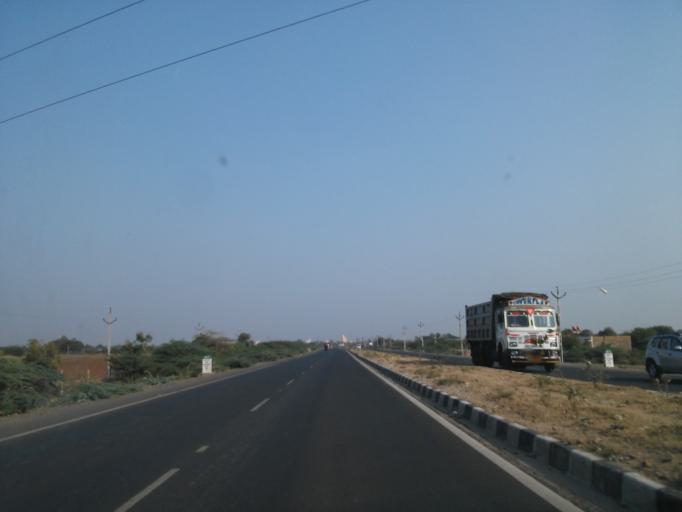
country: IN
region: Gujarat
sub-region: Surendranagar
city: Halvad
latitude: 23.0135
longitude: 71.2143
